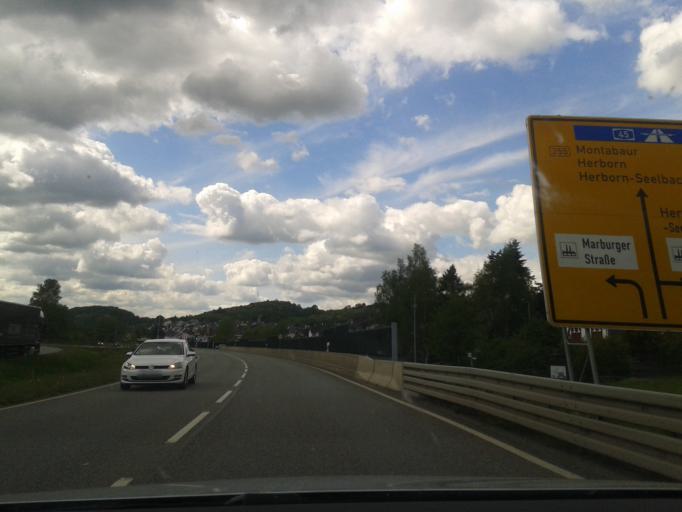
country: DE
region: Hesse
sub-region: Regierungsbezirk Giessen
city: Mittenaar
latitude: 50.6973
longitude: 8.3511
